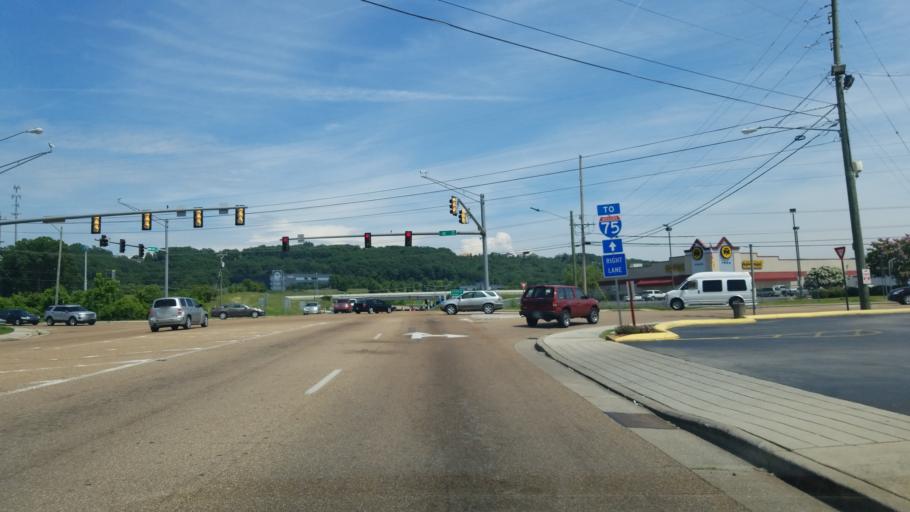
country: US
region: Tennessee
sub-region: Hamilton County
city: Harrison
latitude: 35.0609
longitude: -85.1349
